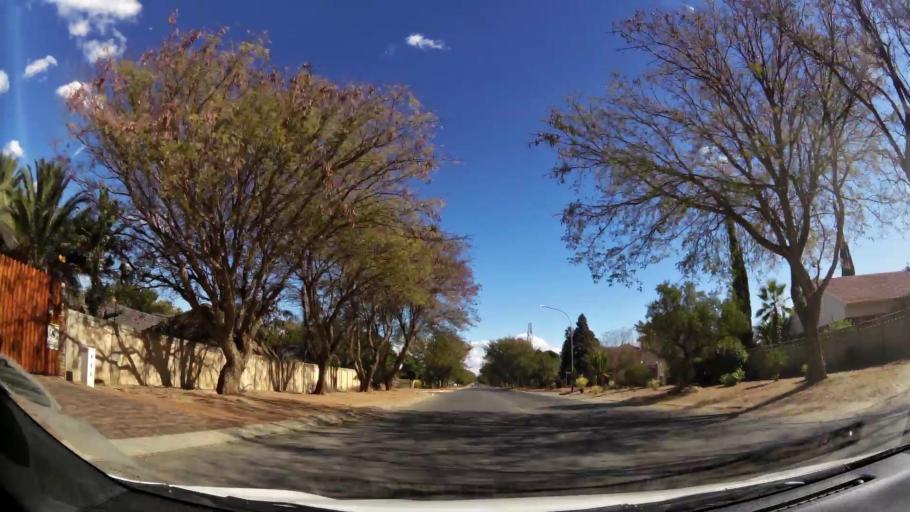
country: ZA
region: Limpopo
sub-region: Capricorn District Municipality
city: Polokwane
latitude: -23.9103
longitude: 29.4824
